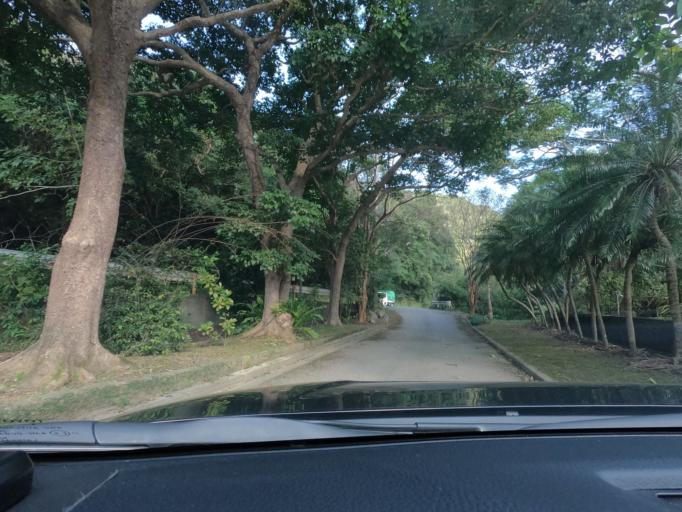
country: JP
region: Okinawa
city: Nago
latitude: 26.7633
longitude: 128.2157
